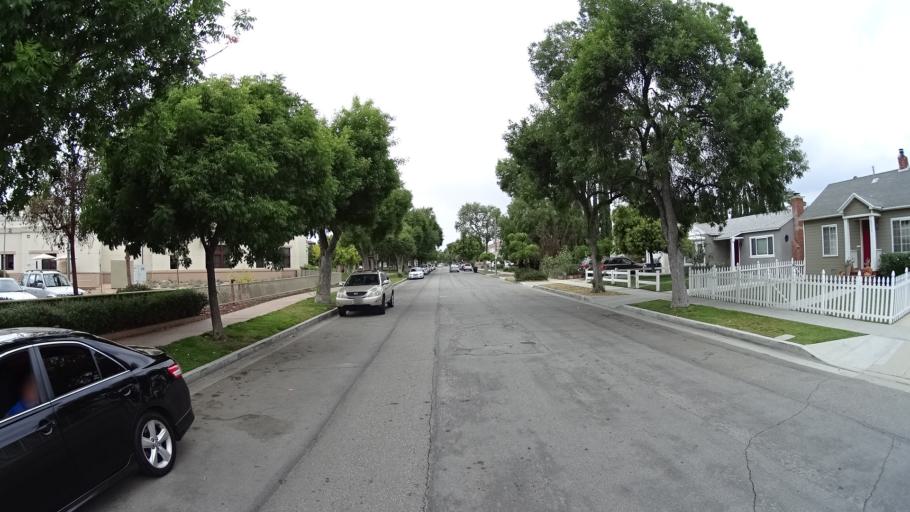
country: US
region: California
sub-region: Los Angeles County
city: Burbank
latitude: 34.1640
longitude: -118.3297
